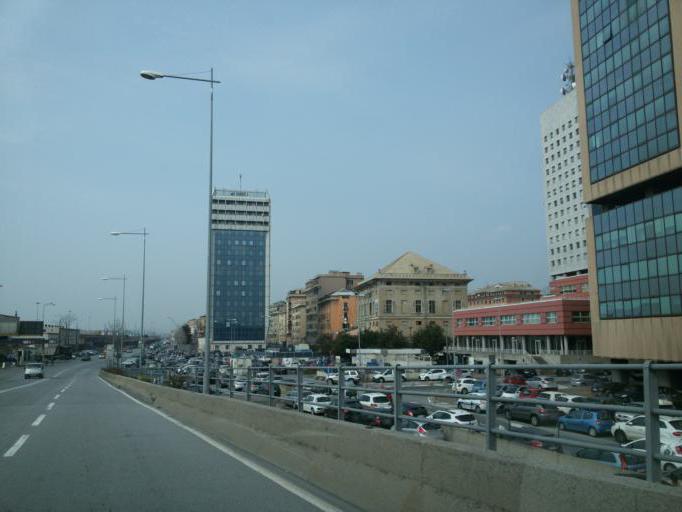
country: IT
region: Liguria
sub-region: Provincia di Genova
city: San Teodoro
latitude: 44.4069
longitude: 8.9000
